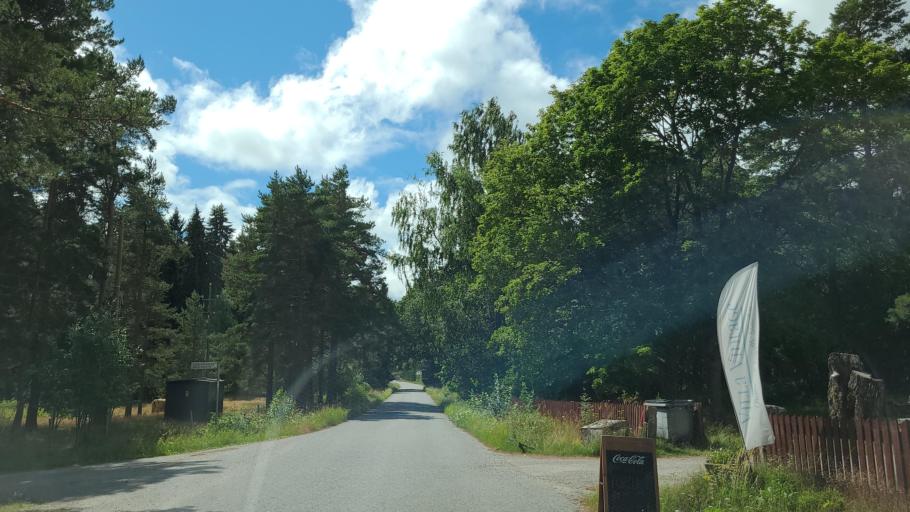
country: FI
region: Varsinais-Suomi
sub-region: Aboland-Turunmaa
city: Nagu
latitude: 60.1688
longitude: 22.0451
